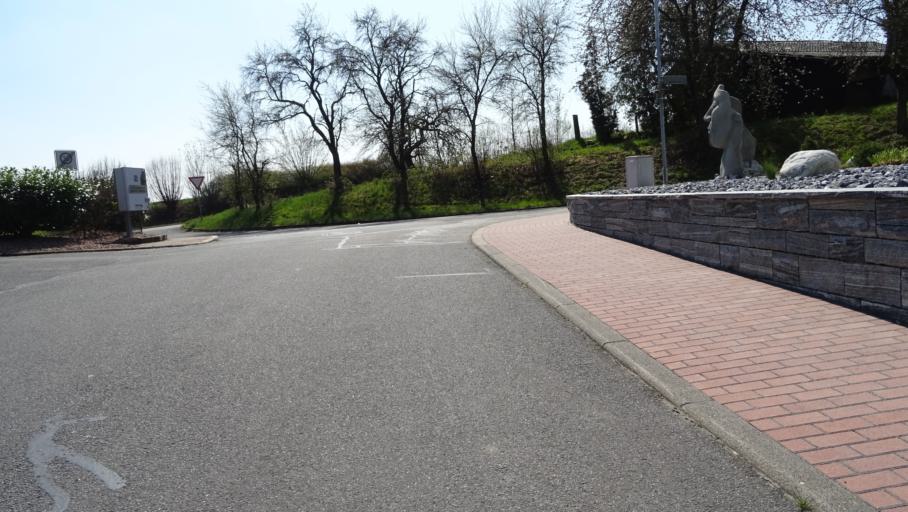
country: DE
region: Baden-Wuerttemberg
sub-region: Karlsruhe Region
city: Seckach
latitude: 49.4126
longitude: 9.2763
